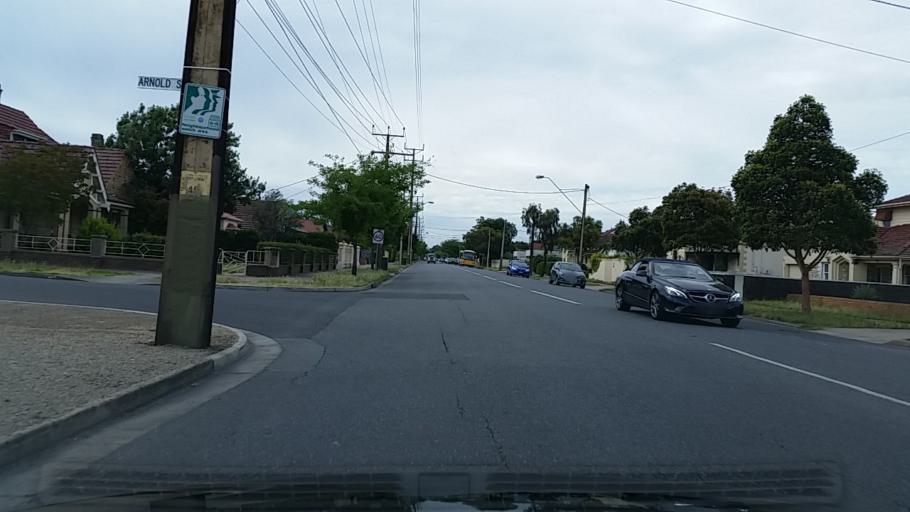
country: AU
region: South Australia
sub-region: City of West Torrens
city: Thebarton
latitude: -34.9237
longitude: 138.5489
